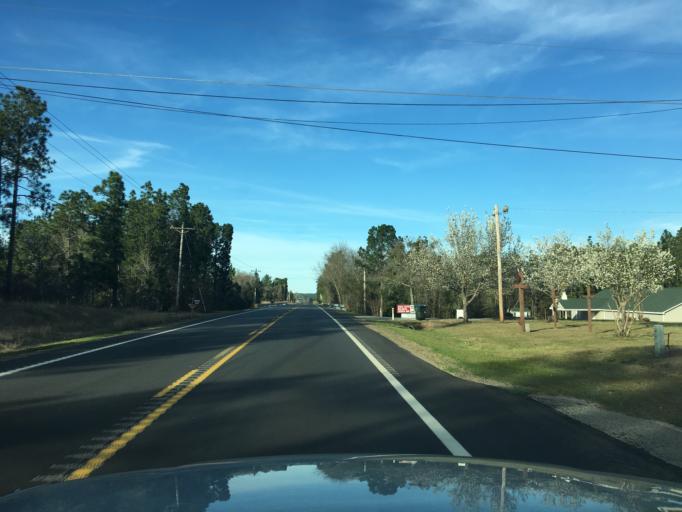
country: US
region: South Carolina
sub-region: Aiken County
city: Aiken
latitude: 33.6856
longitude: -81.6659
